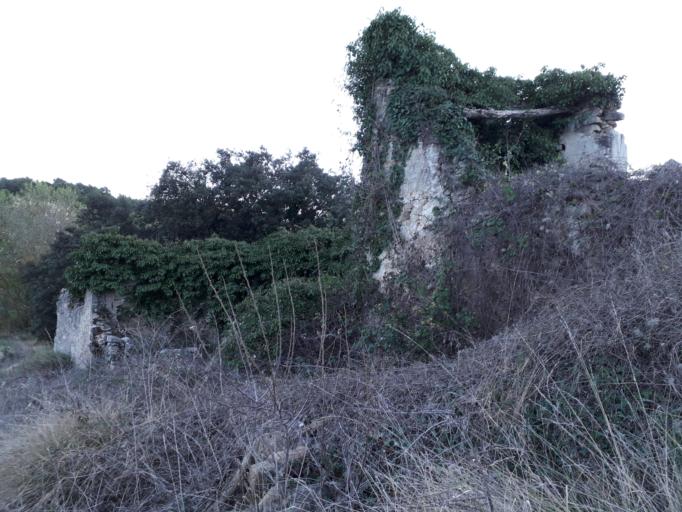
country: ES
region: Catalonia
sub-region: Provincia de Barcelona
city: Bellprat
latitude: 41.5438
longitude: 1.4582
